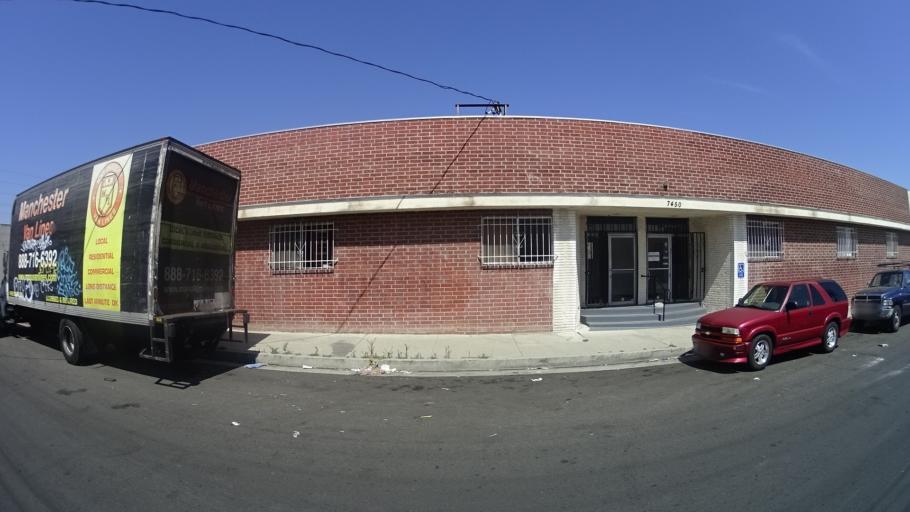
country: US
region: California
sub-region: Los Angeles County
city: Van Nuys
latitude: 34.2063
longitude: -118.4262
